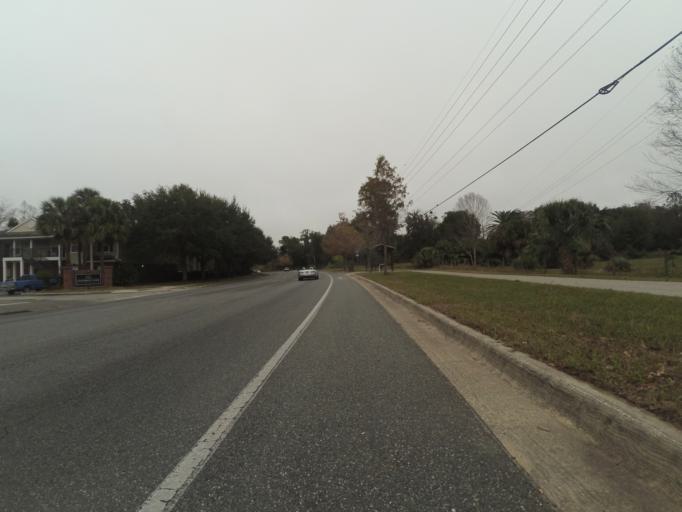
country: US
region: Florida
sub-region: Alachua County
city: Gainesville
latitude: 29.6254
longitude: -82.3562
